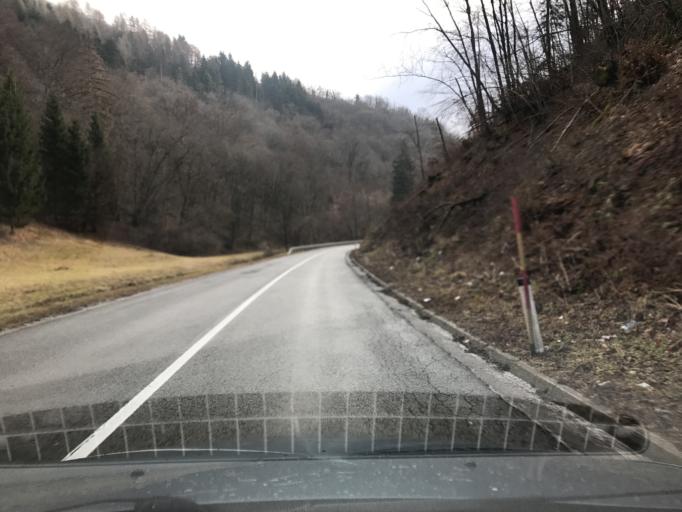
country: SI
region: Gornji Grad
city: Gornji Grad
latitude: 46.2224
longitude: 14.7813
